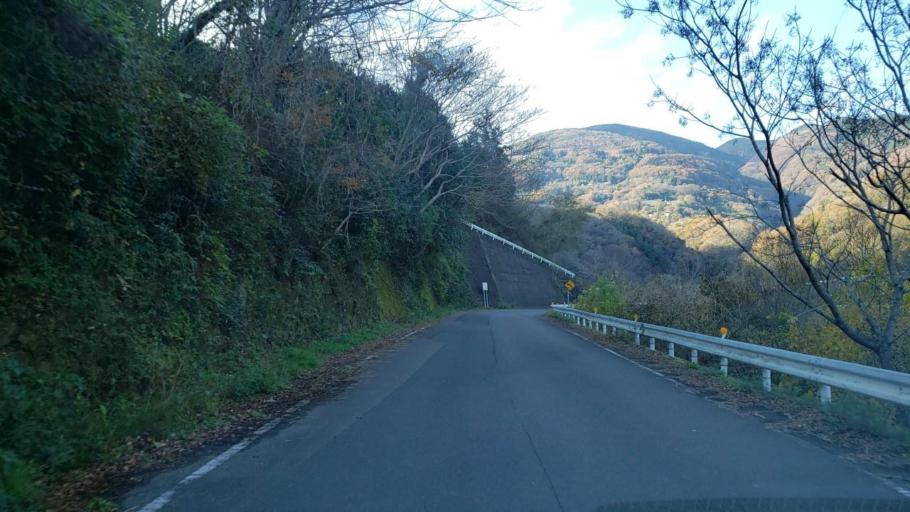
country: JP
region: Tokushima
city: Wakimachi
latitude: 34.0867
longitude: 134.0717
